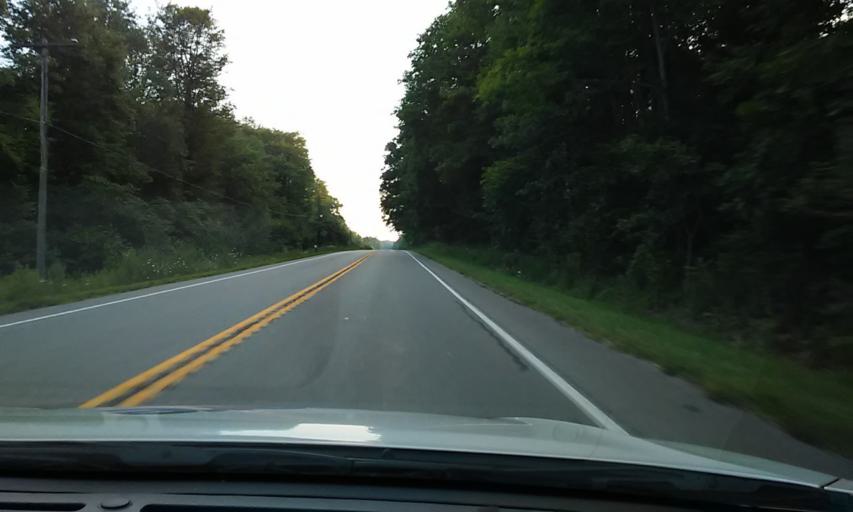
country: US
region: Pennsylvania
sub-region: Forest County
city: Marienville
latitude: 41.4298
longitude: -79.1913
